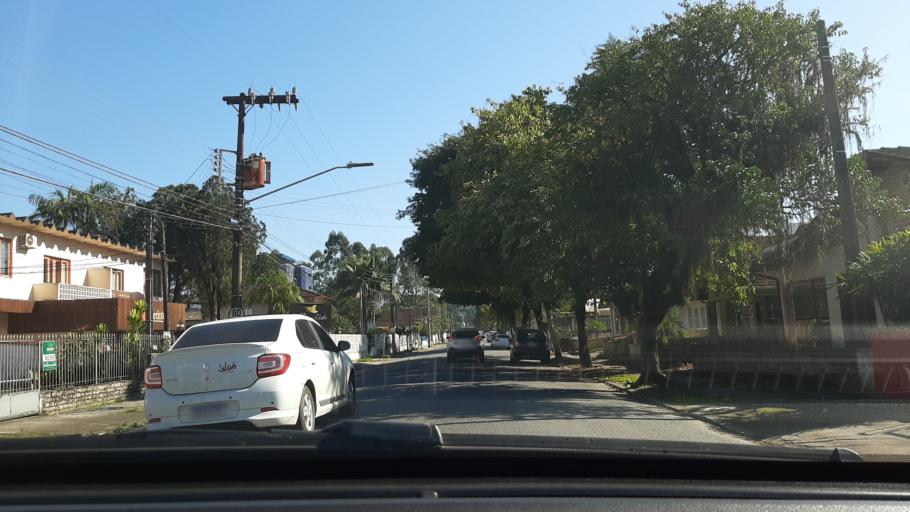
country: BR
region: Santa Catarina
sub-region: Joinville
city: Joinville
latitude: -26.3156
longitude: -48.8496
